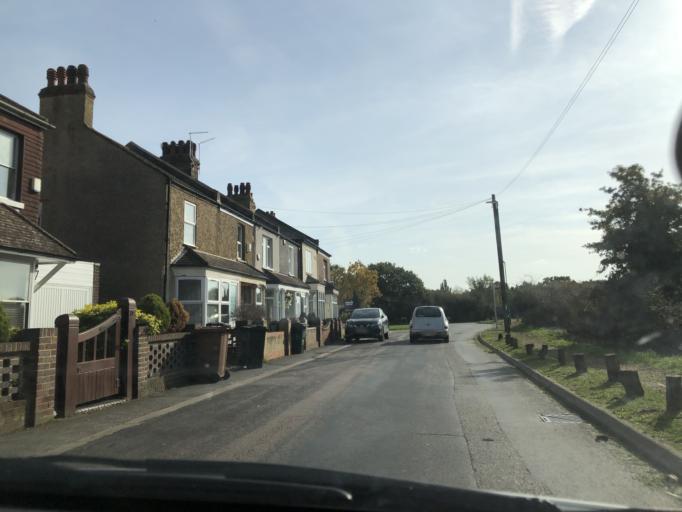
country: GB
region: England
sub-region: Kent
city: Dartford
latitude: 51.4374
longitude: 0.1946
